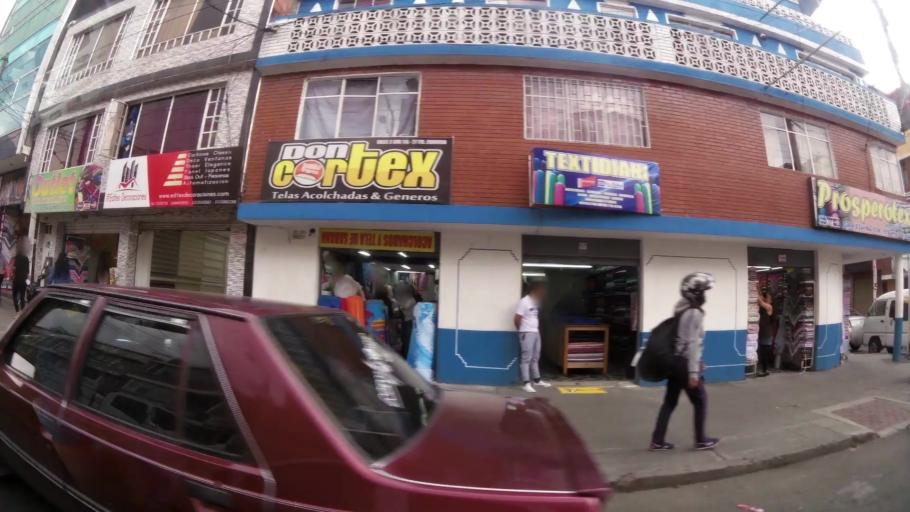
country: CO
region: Bogota D.C.
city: Bogota
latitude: 4.5876
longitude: -74.0890
